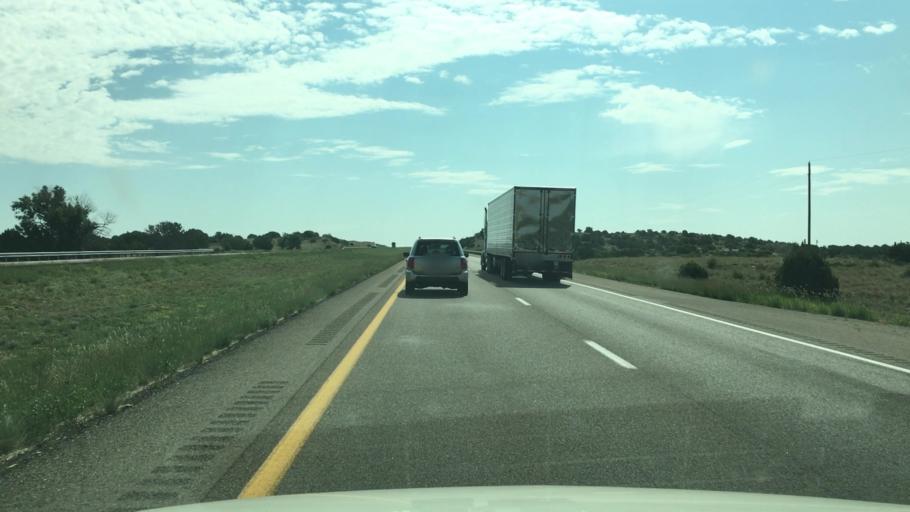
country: US
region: New Mexico
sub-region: Guadalupe County
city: Santa Rosa
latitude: 34.9747
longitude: -104.9592
